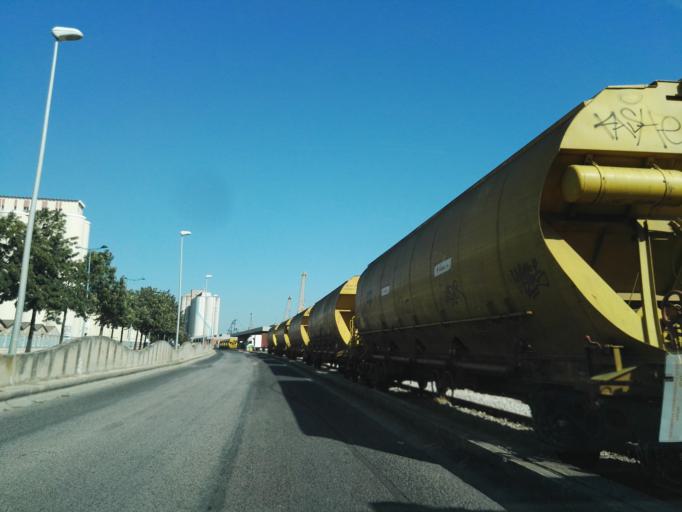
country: PT
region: Lisbon
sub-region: Lisbon
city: Lisbon
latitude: 38.7289
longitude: -9.1070
